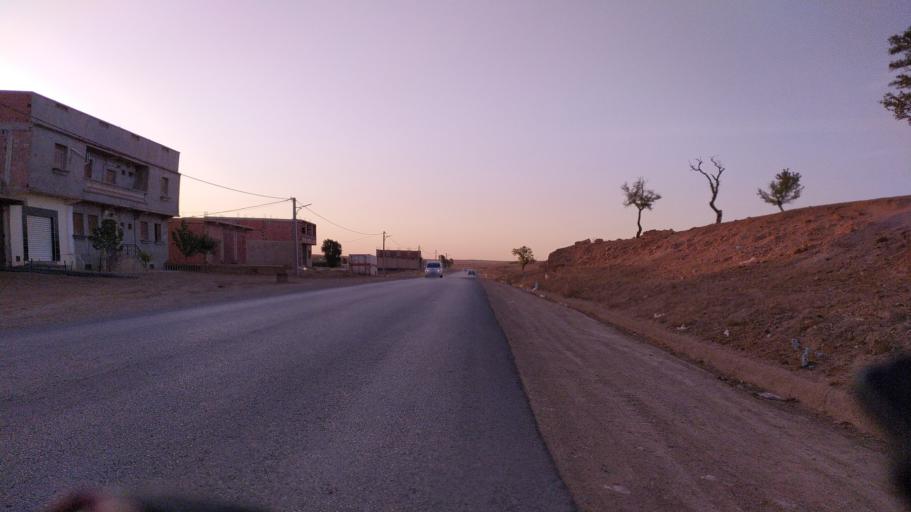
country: DZ
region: Tiaret
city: Frenda
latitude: 34.8990
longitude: 1.2458
